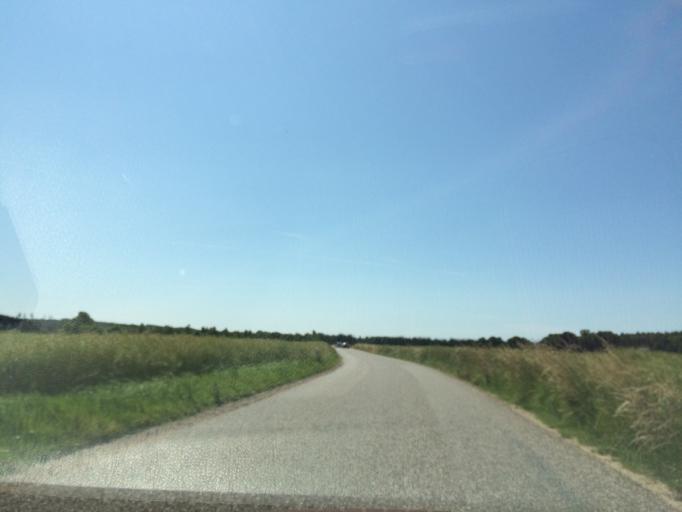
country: DK
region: Central Jutland
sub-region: Silkeborg Kommune
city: Svejbaek
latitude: 56.2464
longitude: 9.6770
